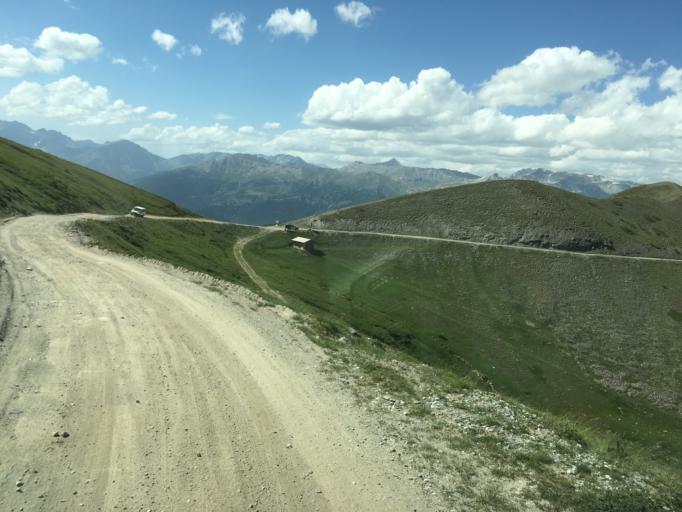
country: IT
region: Piedmont
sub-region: Provincia di Torino
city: Sestriere
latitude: 44.9868
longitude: 6.8700
